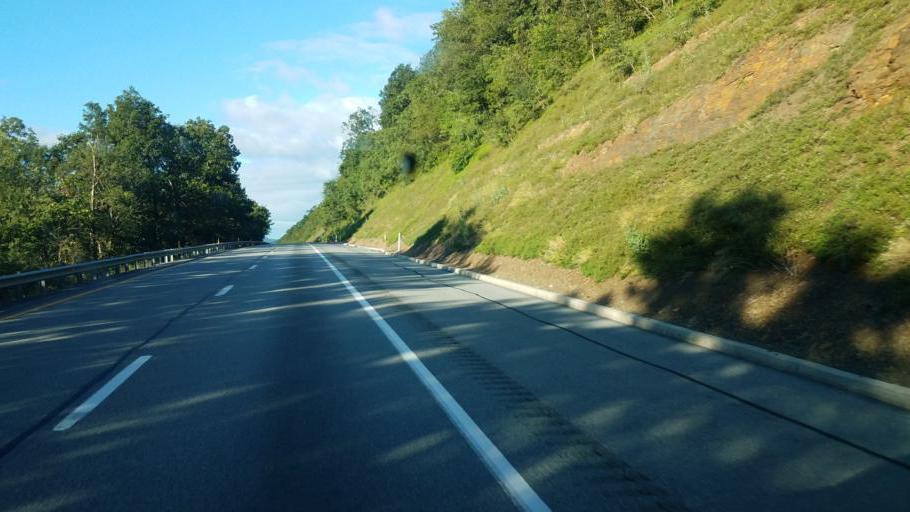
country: US
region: Pennsylvania
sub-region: Bedford County
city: Earlston
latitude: 39.8808
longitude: -78.2457
